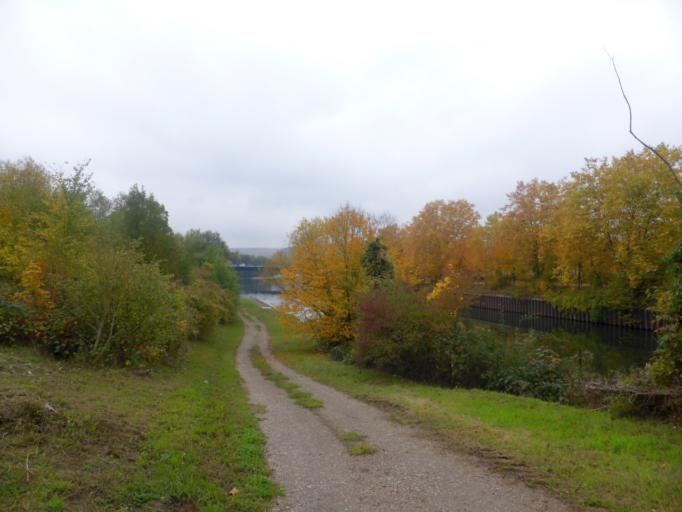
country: FR
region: Lorraine
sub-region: Departement de Meurthe-et-Moselle
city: Frouard
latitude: 48.7778
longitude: 6.1367
